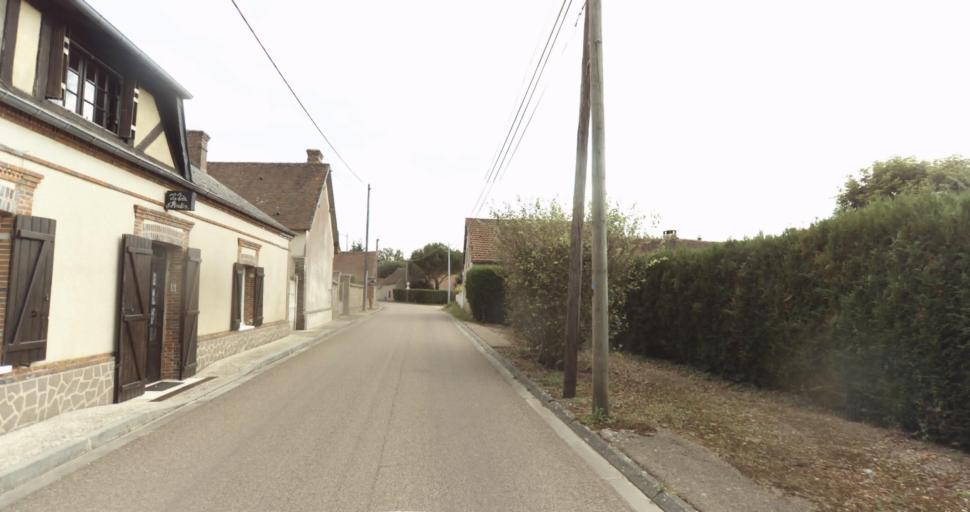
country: FR
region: Haute-Normandie
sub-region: Departement de l'Eure
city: Nonancourt
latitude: 48.8348
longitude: 1.1671
